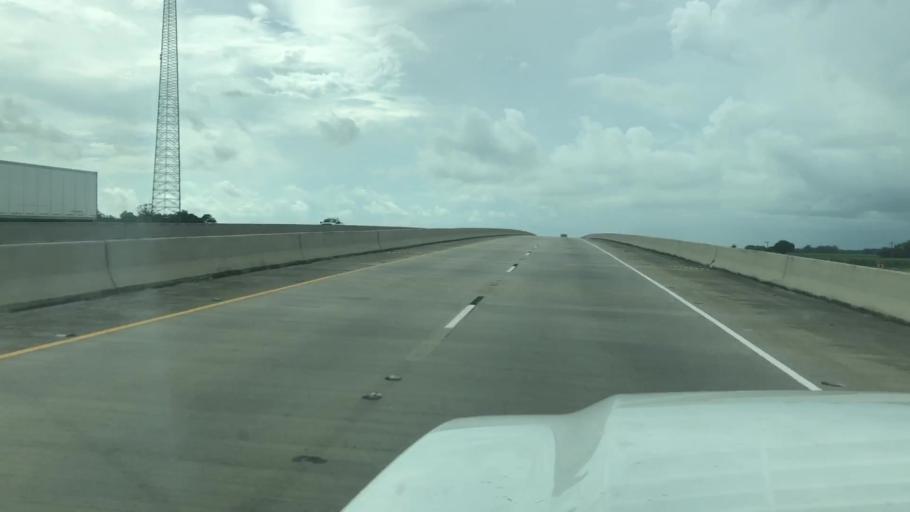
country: US
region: Louisiana
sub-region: Iberia Parish
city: Jeanerette
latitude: 29.9186
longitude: -91.7267
